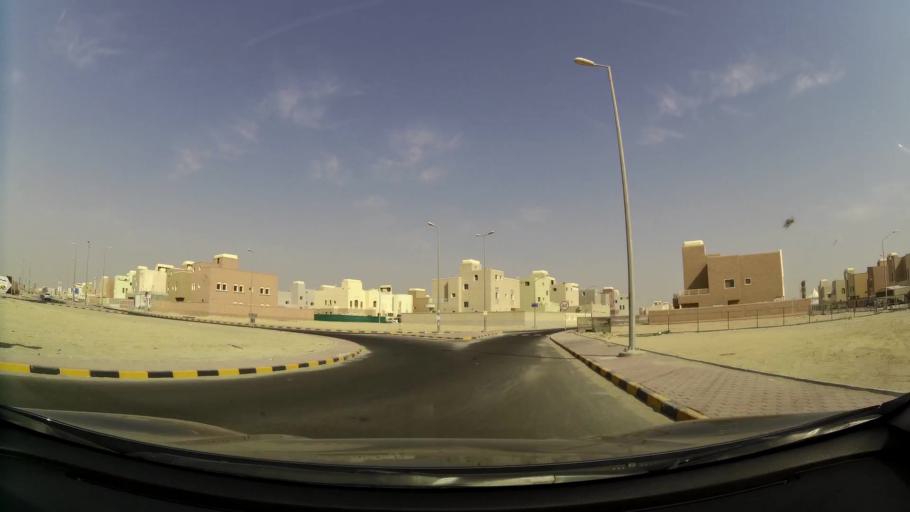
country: KW
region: Al Ahmadi
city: Al Wafrah
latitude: 28.8015
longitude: 48.0676
